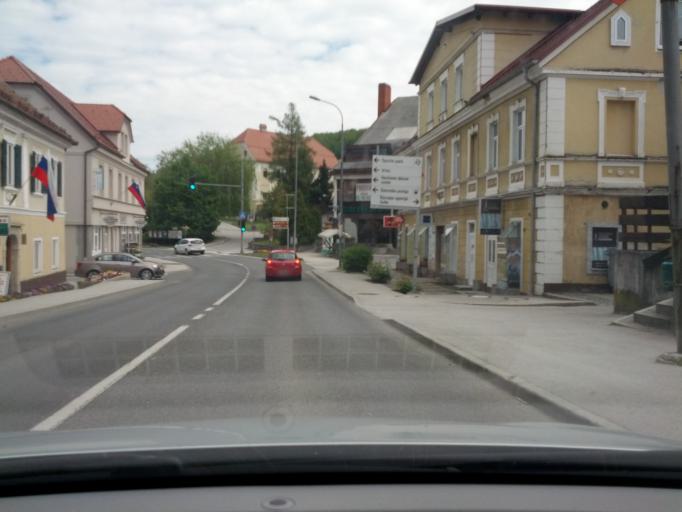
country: SI
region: Smarje pri Jelsah
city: Smarje pri Jelsah
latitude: 46.2288
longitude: 15.5184
